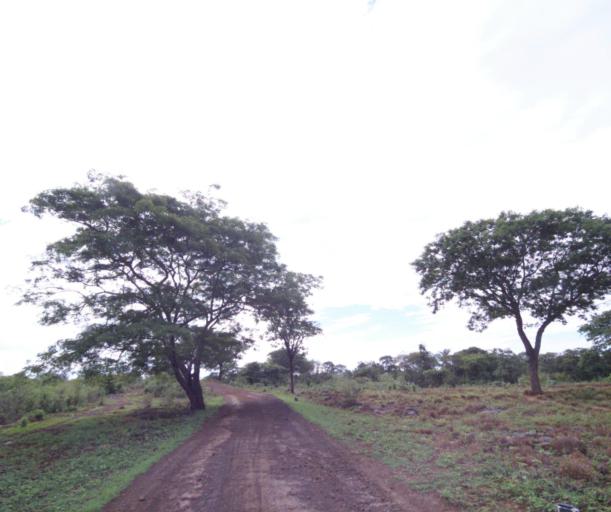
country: BR
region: Bahia
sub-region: Carinhanha
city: Carinhanha
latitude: -14.2275
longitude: -44.4332
